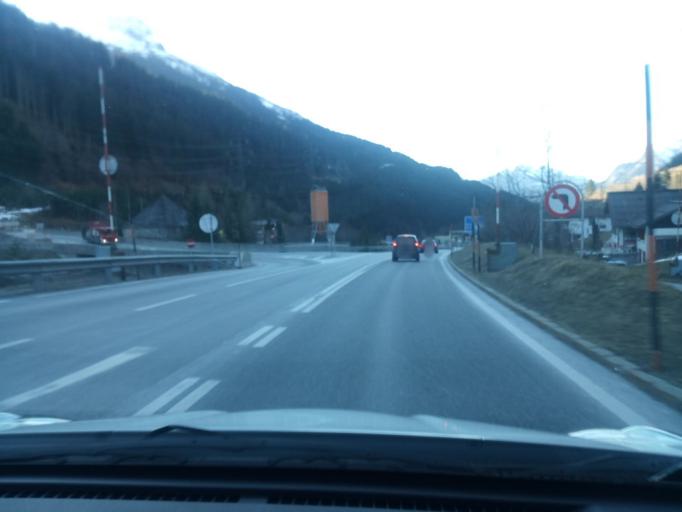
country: AT
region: Vorarlberg
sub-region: Politischer Bezirk Bludenz
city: Klosterle
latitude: 47.1321
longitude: 10.1156
